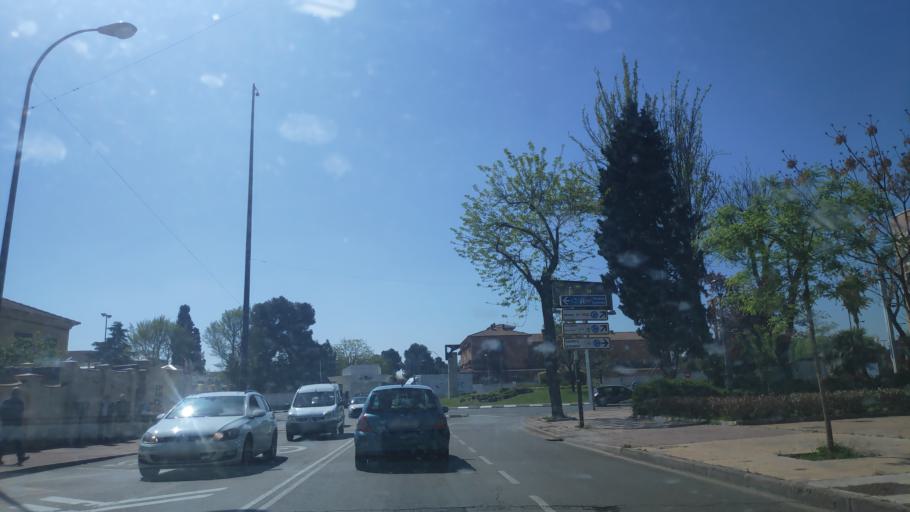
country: ES
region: Madrid
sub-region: Provincia de Madrid
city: Getafe
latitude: 40.3051
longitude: -3.7249
